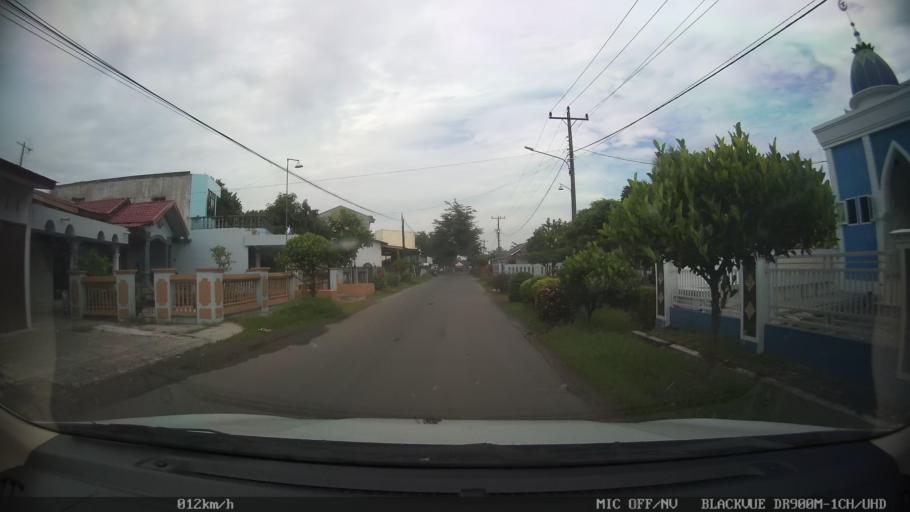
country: ID
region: North Sumatra
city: Sunggal
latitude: 3.6542
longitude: 98.5959
